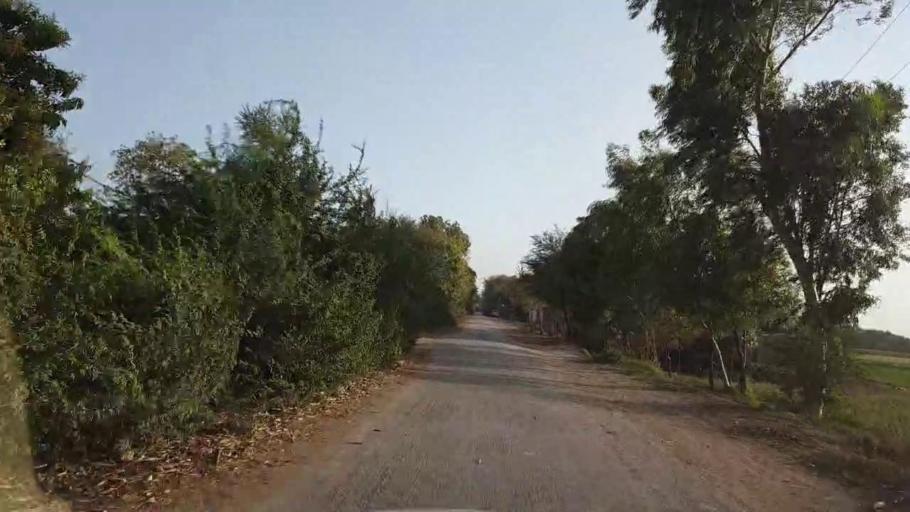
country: PK
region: Sindh
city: Tando Ghulam Ali
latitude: 25.1229
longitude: 68.9069
